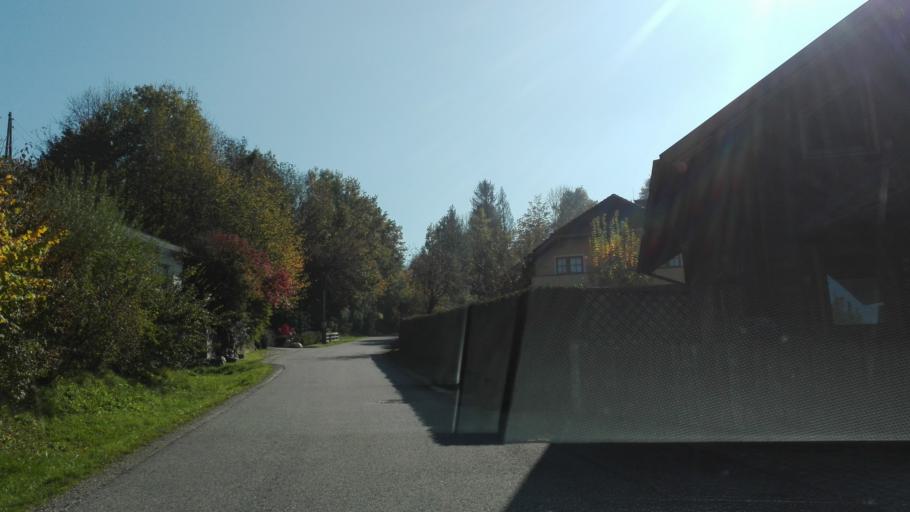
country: AT
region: Upper Austria
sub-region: Politischer Bezirk Urfahr-Umgebung
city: Ottensheim
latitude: 48.3080
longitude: 14.1757
